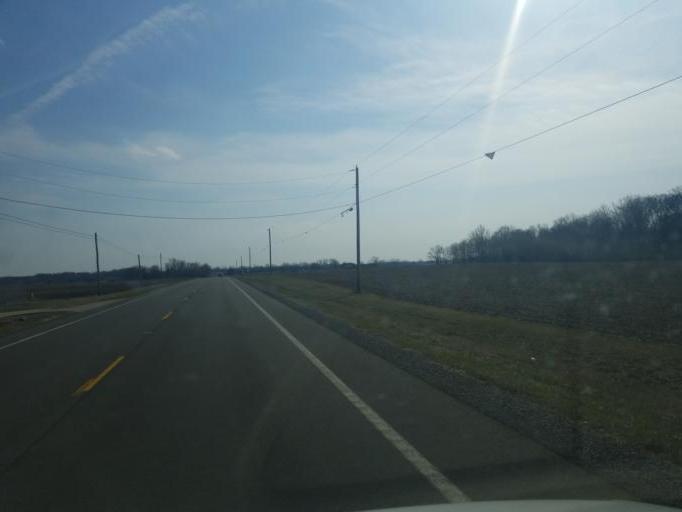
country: US
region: Ohio
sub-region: Logan County
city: Northwood
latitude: 40.5132
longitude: -83.6904
